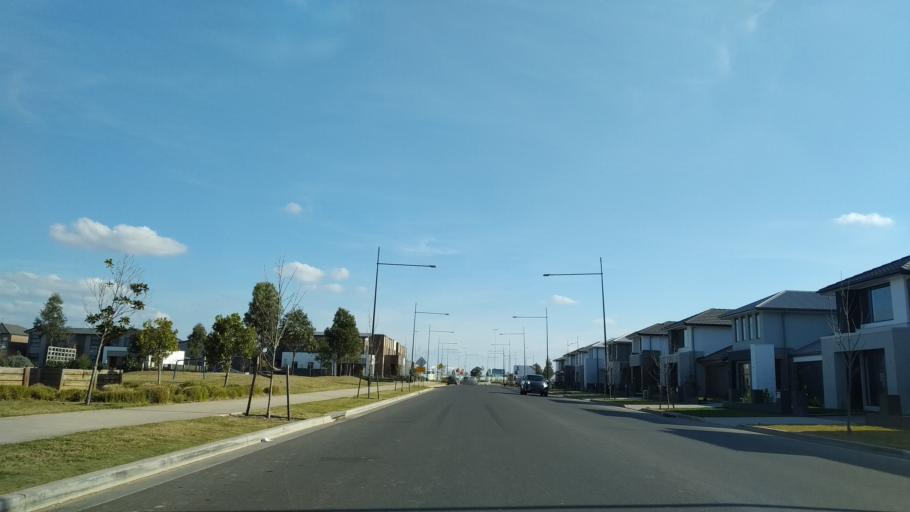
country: AU
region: New South Wales
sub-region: Blacktown
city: Hassall Grove
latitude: -33.6935
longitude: 150.8225
